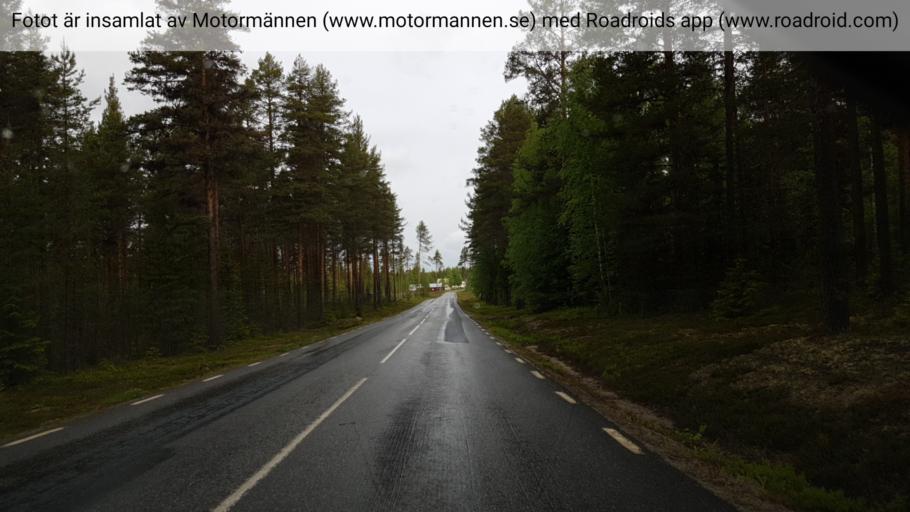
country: SE
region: Vaesterbotten
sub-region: Norsjo Kommun
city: Norsjoe
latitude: 64.6483
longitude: 19.2796
